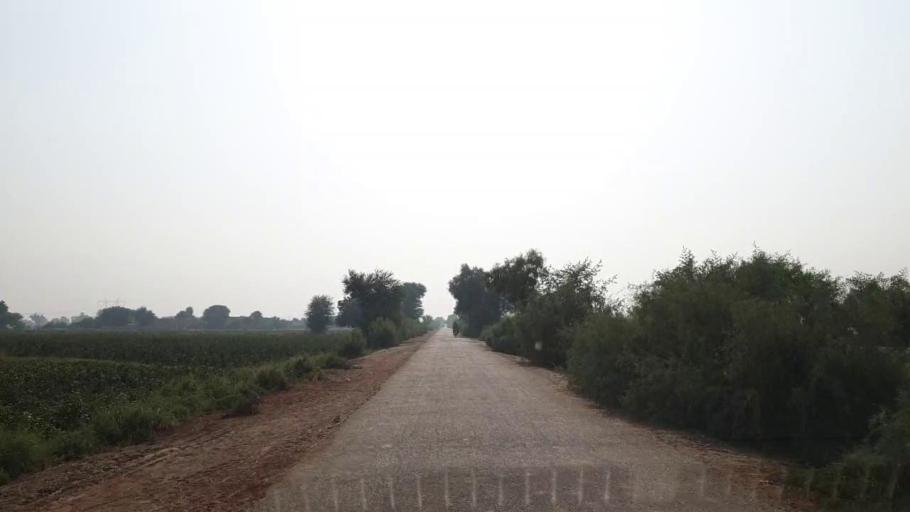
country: PK
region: Sindh
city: Bhan
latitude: 26.4814
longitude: 67.7699
